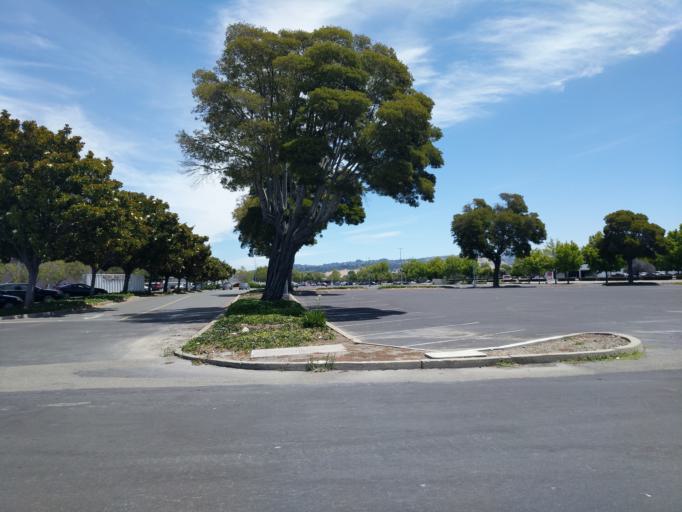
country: US
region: California
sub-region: Alameda County
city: Cherryland
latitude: 37.6488
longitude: -122.1059
